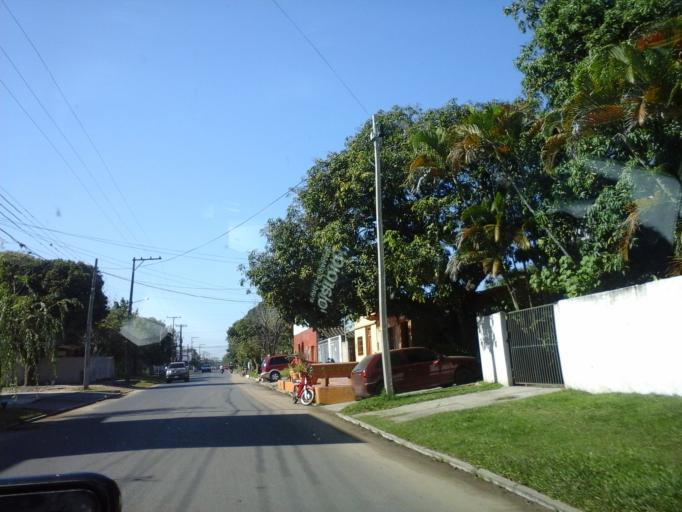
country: PY
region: Neembucu
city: Pilar
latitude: -26.8623
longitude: -58.3050
